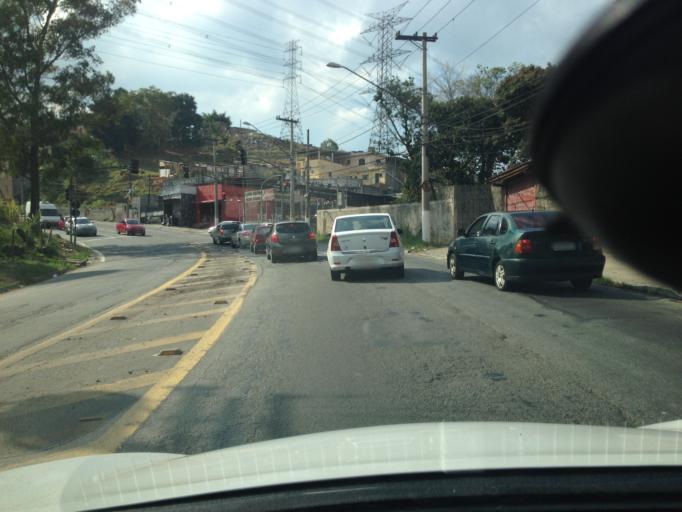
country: BR
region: Sao Paulo
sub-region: Caieiras
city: Caieiras
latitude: -23.4592
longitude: -46.7191
